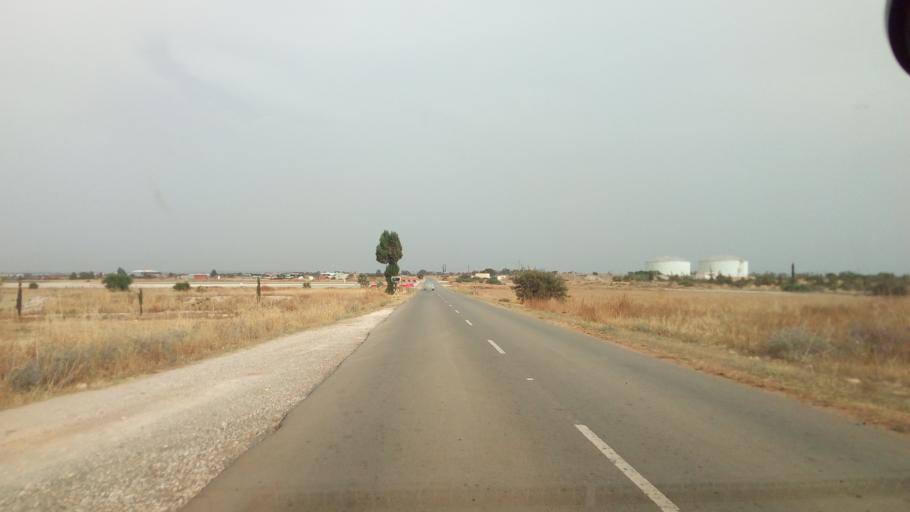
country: CY
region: Larnaka
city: Pyla
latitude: 35.0130
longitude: 33.7088
